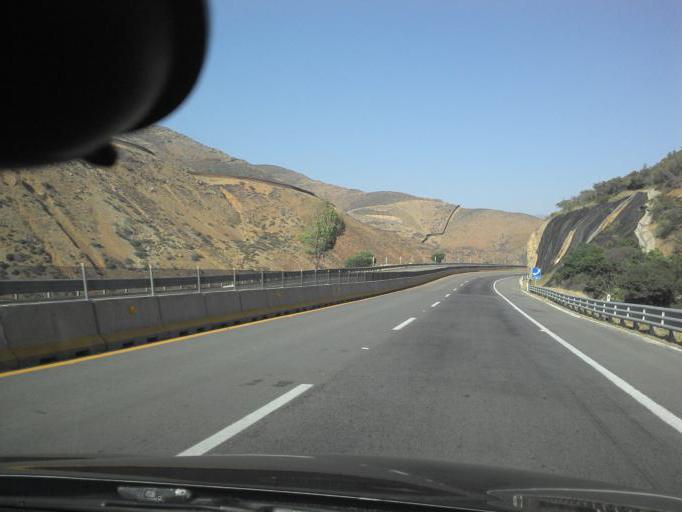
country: MX
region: Baja California
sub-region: Tijuana
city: El Nino
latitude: 32.5580
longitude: -116.8163
